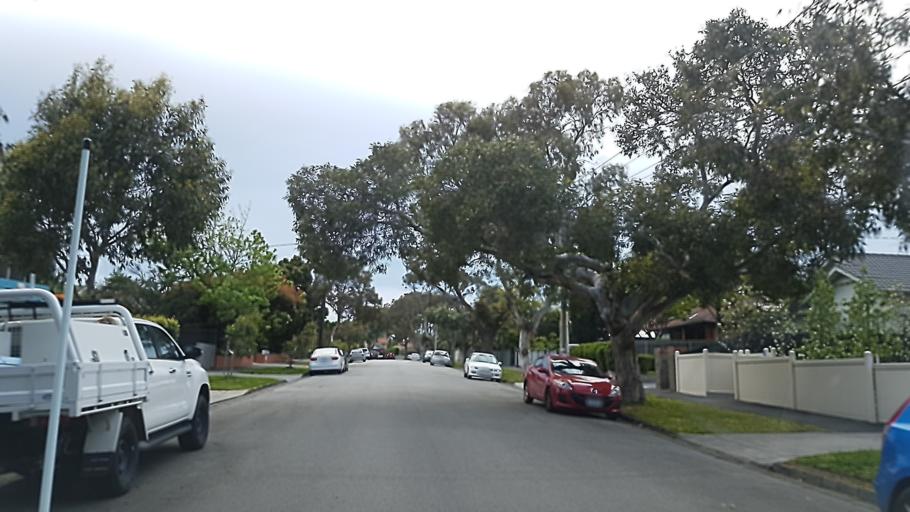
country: AU
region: Victoria
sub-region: Stonnington
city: Malvern East
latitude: -37.8719
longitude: 145.0525
